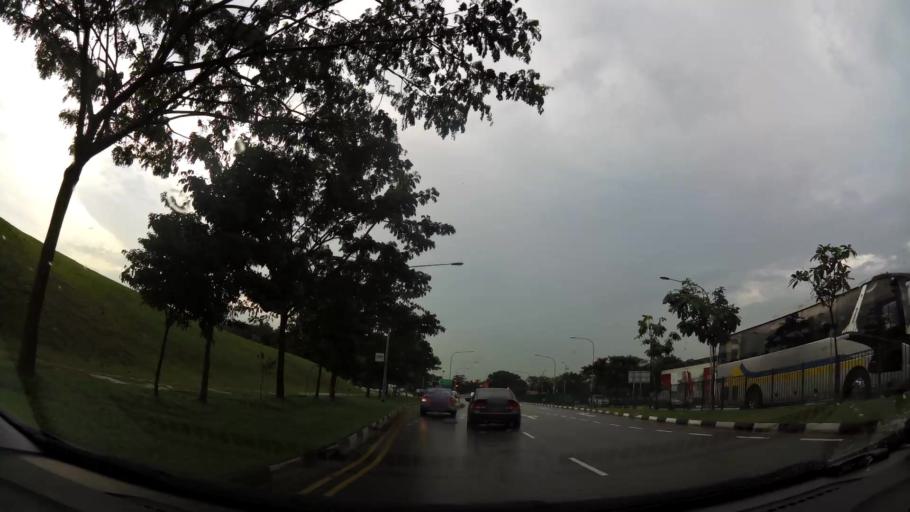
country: MY
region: Johor
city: Kampung Pasir Gudang Baru
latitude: 1.3911
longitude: 103.8702
